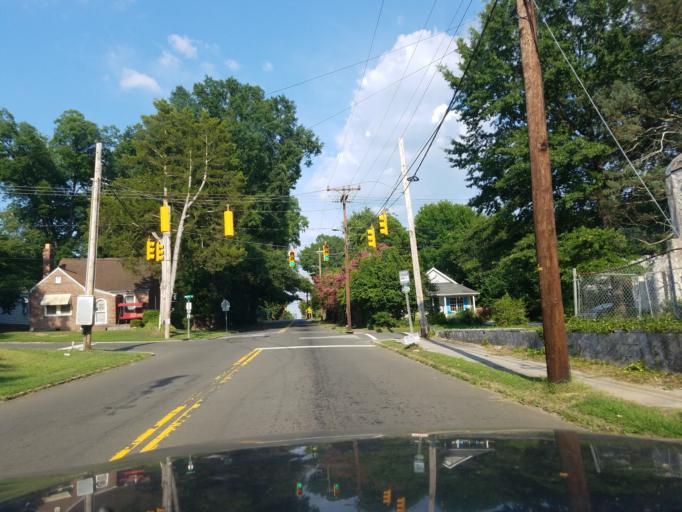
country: US
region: North Carolina
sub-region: Durham County
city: Durham
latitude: 35.9917
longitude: -78.9147
